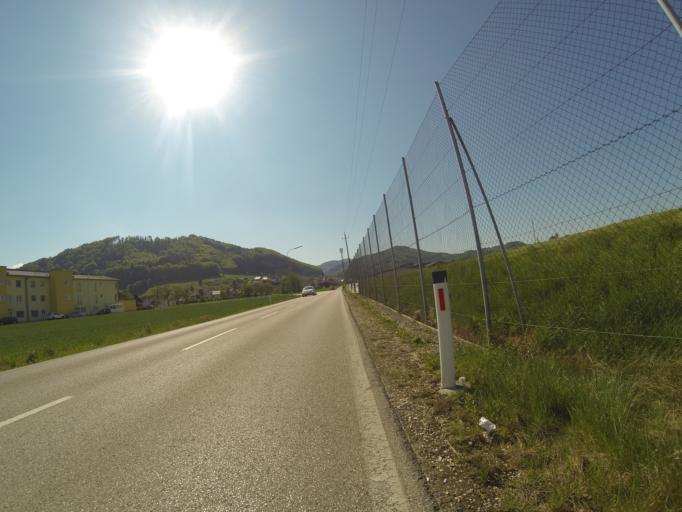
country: AT
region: Upper Austria
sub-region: Politischer Bezirk Gmunden
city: Gmunden
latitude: 47.9304
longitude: 13.7772
